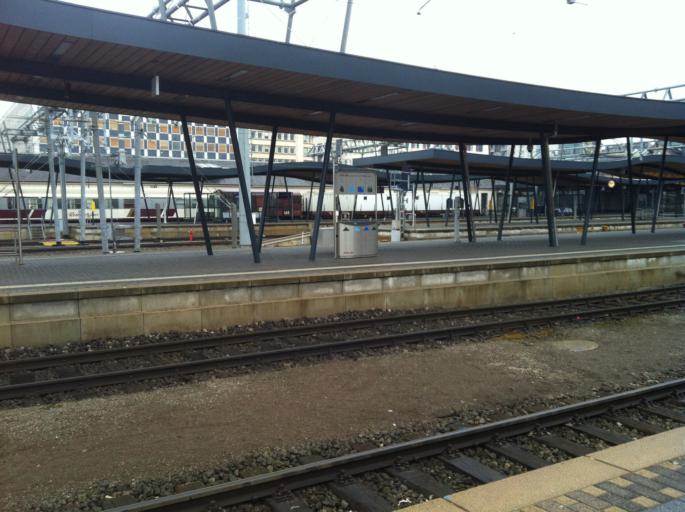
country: LU
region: Luxembourg
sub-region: Canton de Luxembourg
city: Luxembourg
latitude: 49.5983
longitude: 6.1342
